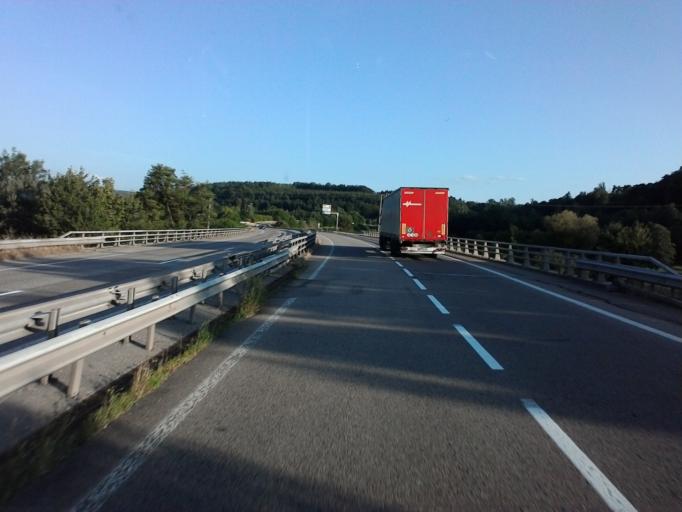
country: FR
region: Lorraine
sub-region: Departement des Vosges
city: Arches
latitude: 48.1290
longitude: 6.5151
